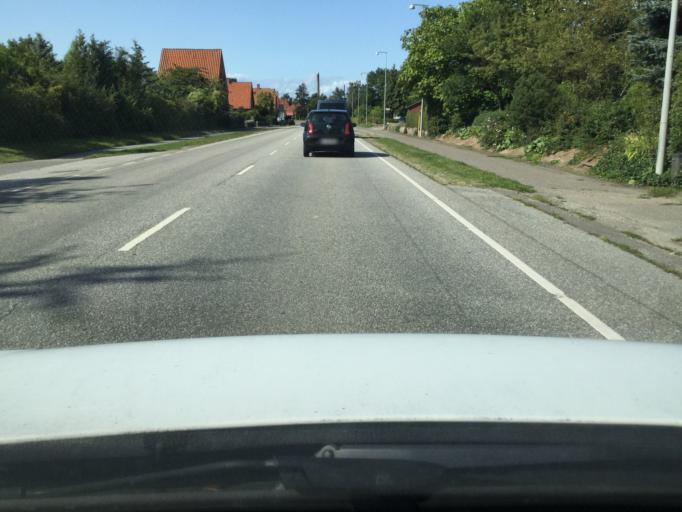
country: DK
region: Zealand
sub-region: Lolland Kommune
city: Nakskov
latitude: 54.8206
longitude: 11.1560
